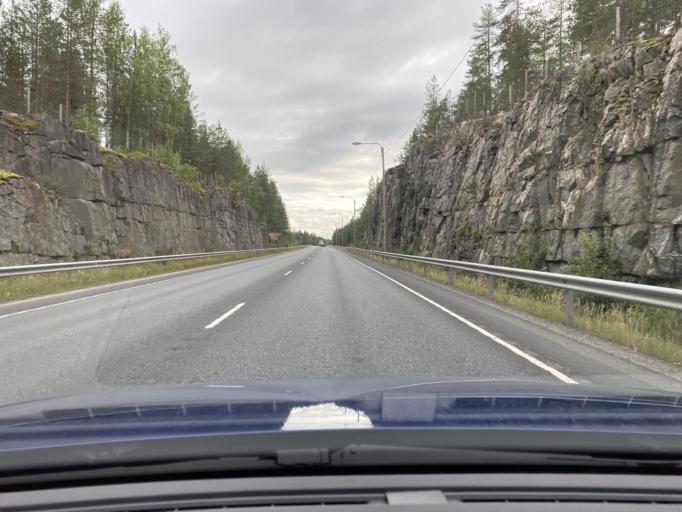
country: FI
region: Pirkanmaa
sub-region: Tampere
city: Kangasala
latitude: 61.5671
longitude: 24.1028
